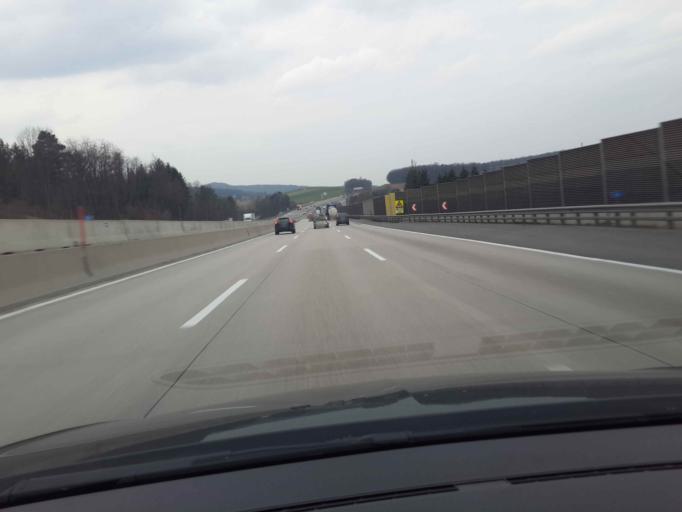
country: AT
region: Lower Austria
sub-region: Politischer Bezirk Sankt Polten
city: Kirchstetten
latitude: 48.1730
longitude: 15.8526
